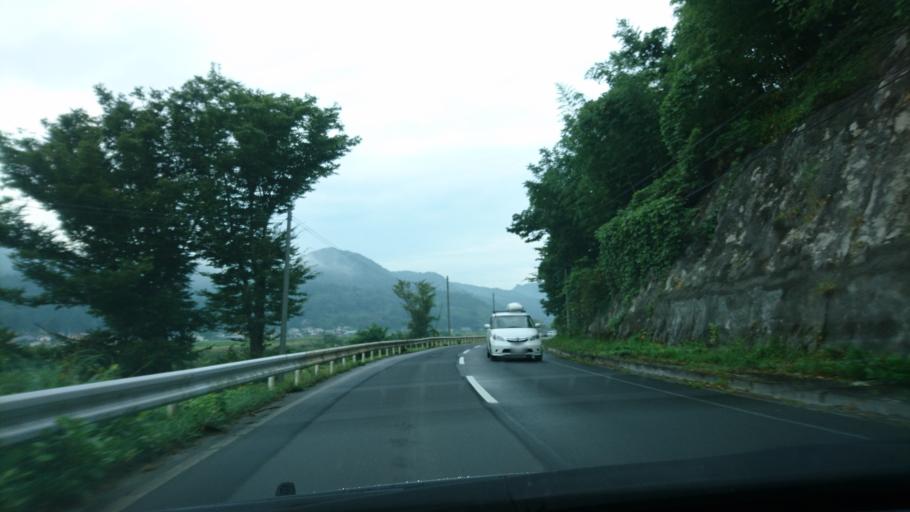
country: JP
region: Iwate
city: Ichinoseki
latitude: 38.9630
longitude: 141.2460
